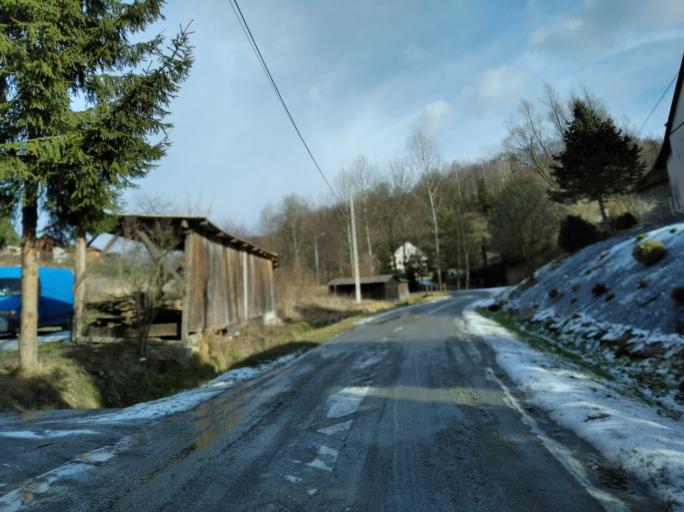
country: PL
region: Subcarpathian Voivodeship
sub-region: Powiat strzyzowski
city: Strzyzow
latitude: 49.9013
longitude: 21.7522
